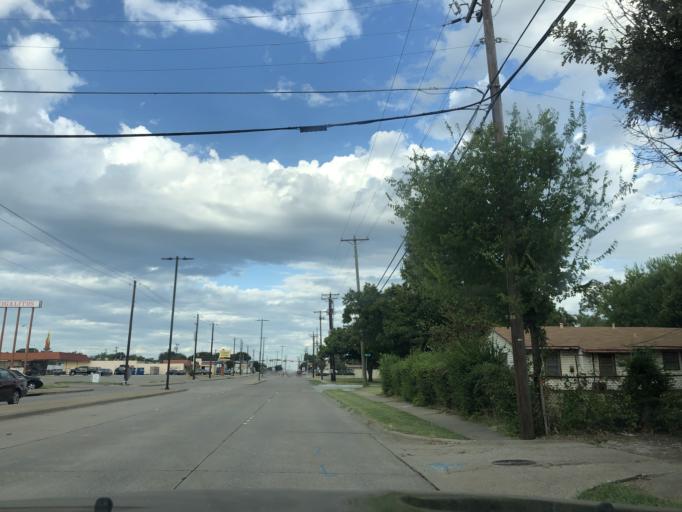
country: US
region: Texas
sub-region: Dallas County
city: Garland
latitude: 32.8789
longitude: -96.6450
